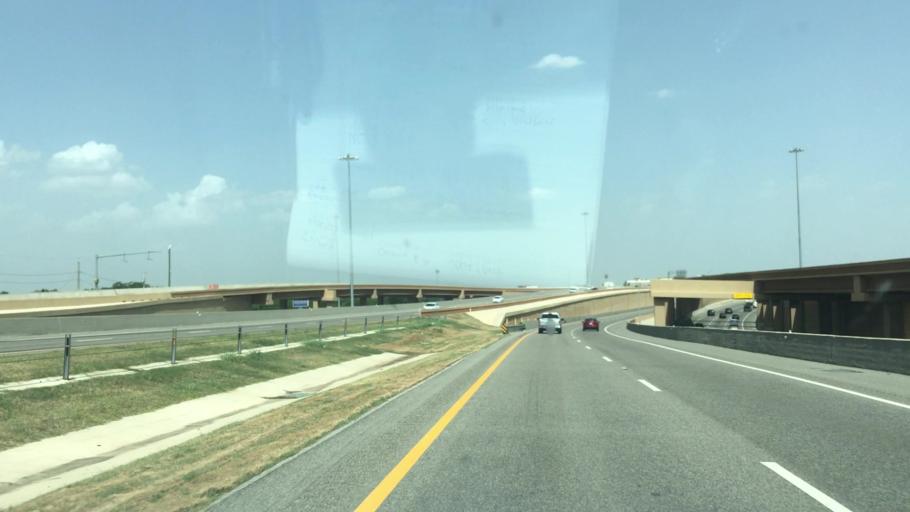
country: US
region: Texas
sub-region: Tarrant County
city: Bedford
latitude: 32.8400
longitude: -97.1557
